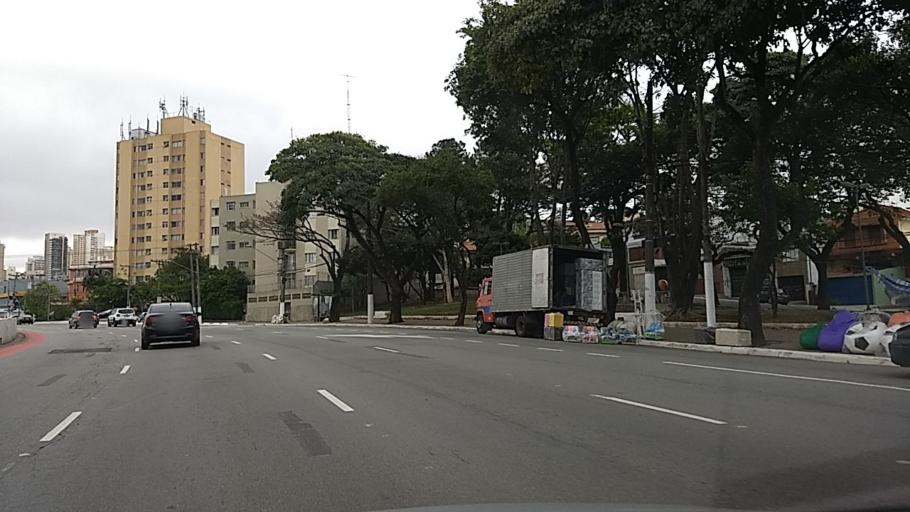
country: BR
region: Sao Paulo
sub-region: Sao Paulo
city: Sao Paulo
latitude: -23.5838
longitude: -46.6174
